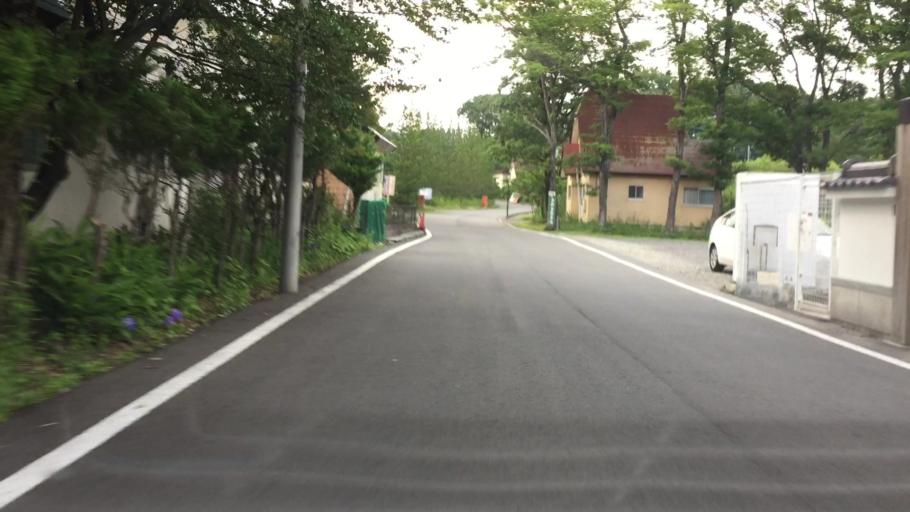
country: JP
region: Tochigi
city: Kuroiso
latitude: 37.0404
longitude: 140.0276
